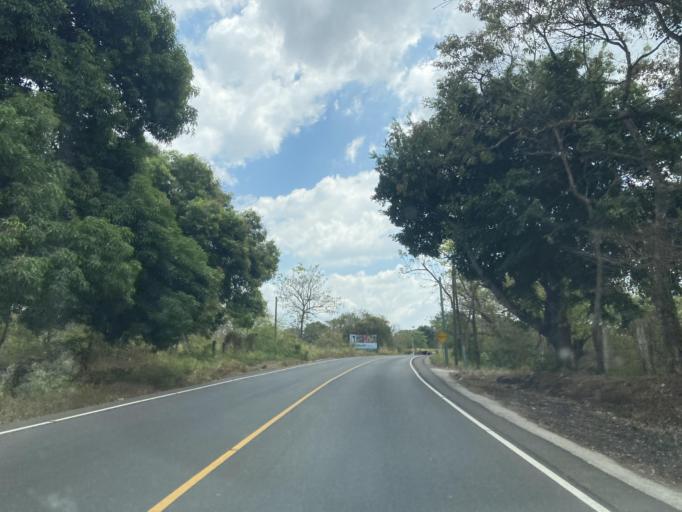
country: GT
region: Santa Rosa
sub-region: Municipio de Taxisco
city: Taxisco
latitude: 14.0895
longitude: -90.4998
